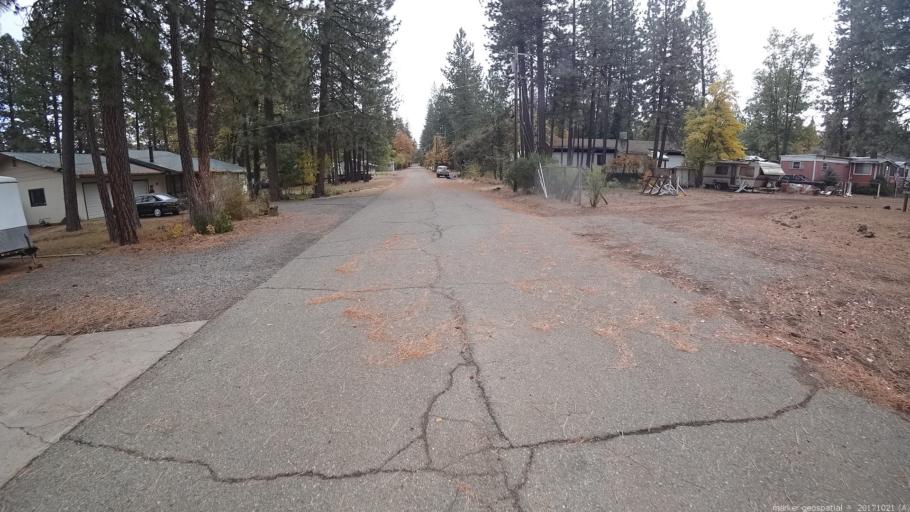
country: US
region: California
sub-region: Shasta County
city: Burney
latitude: 40.9200
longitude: -121.6306
